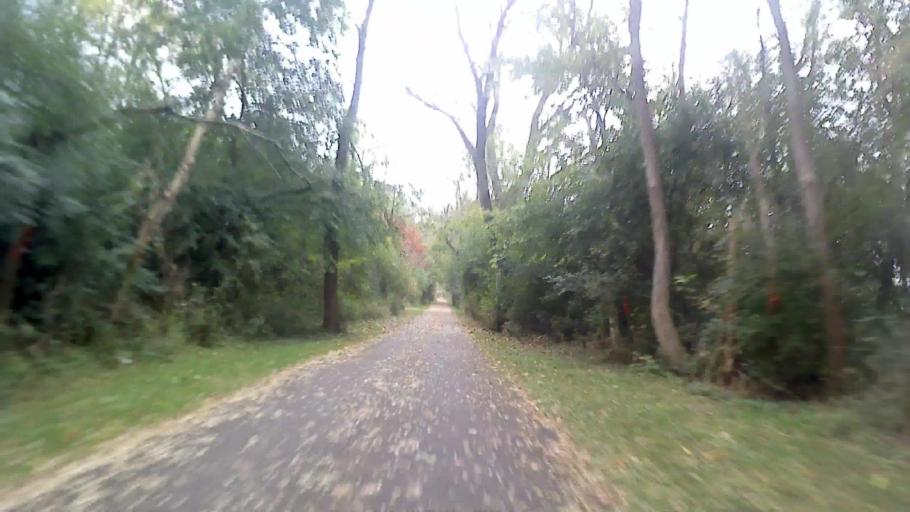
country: US
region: Illinois
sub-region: Kane County
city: Sugar Grove
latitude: 41.7720
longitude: -88.4105
